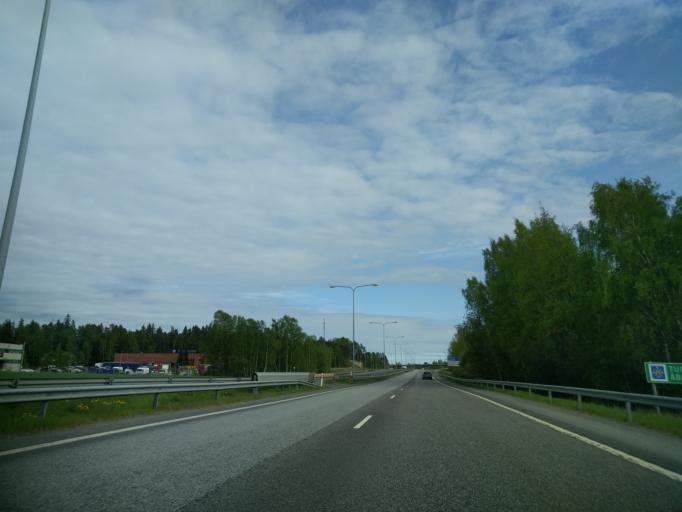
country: FI
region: Varsinais-Suomi
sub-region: Turku
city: Raisio
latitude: 60.4695
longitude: 22.1982
